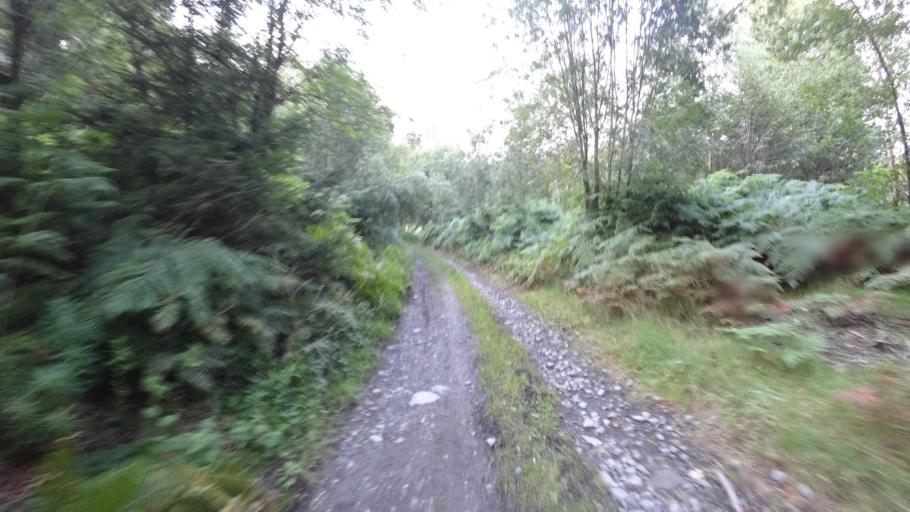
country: BE
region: Wallonia
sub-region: Province du Luxembourg
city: Neufchateau
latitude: 49.8729
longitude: 5.3777
